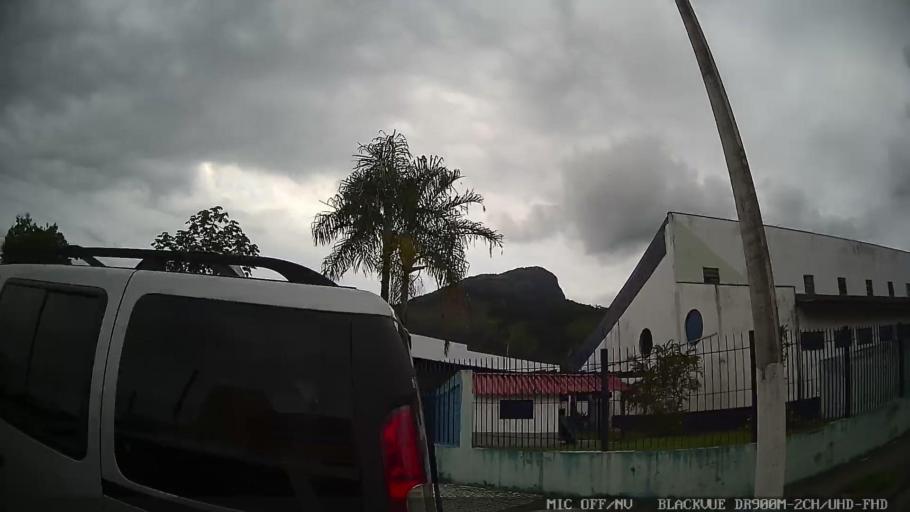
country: BR
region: Sao Paulo
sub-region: Caraguatatuba
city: Caraguatatuba
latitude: -23.6289
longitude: -45.4354
